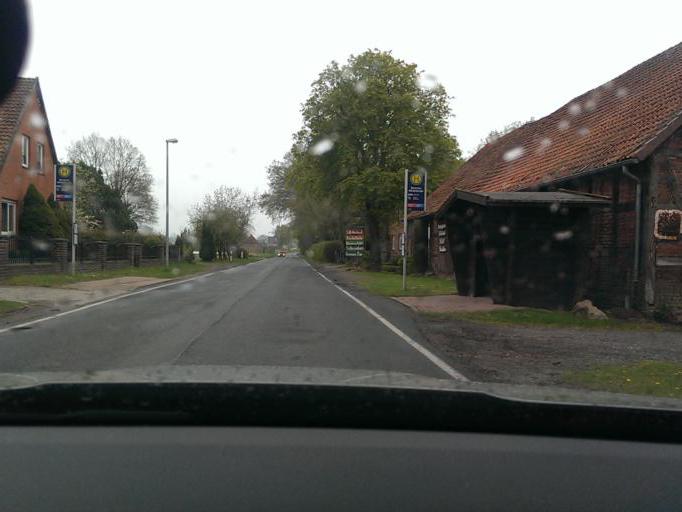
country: DE
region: Lower Saxony
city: Steimbke
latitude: 52.6178
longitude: 9.4849
